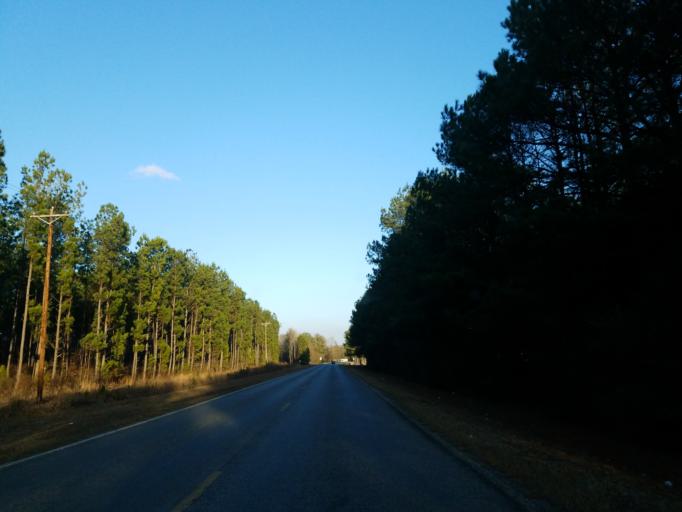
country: US
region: Mississippi
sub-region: Clarke County
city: Stonewall
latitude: 32.1690
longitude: -88.8435
